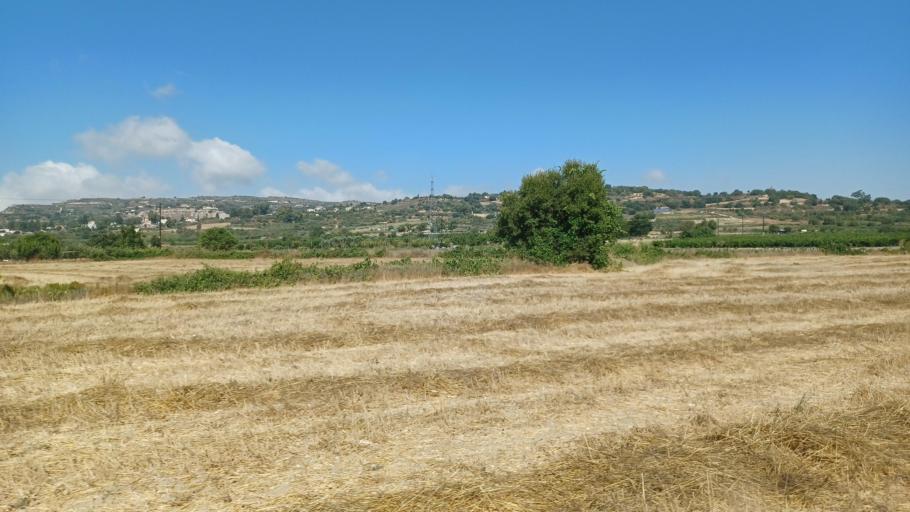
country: CY
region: Pafos
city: Tala
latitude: 34.8852
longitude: 32.4958
